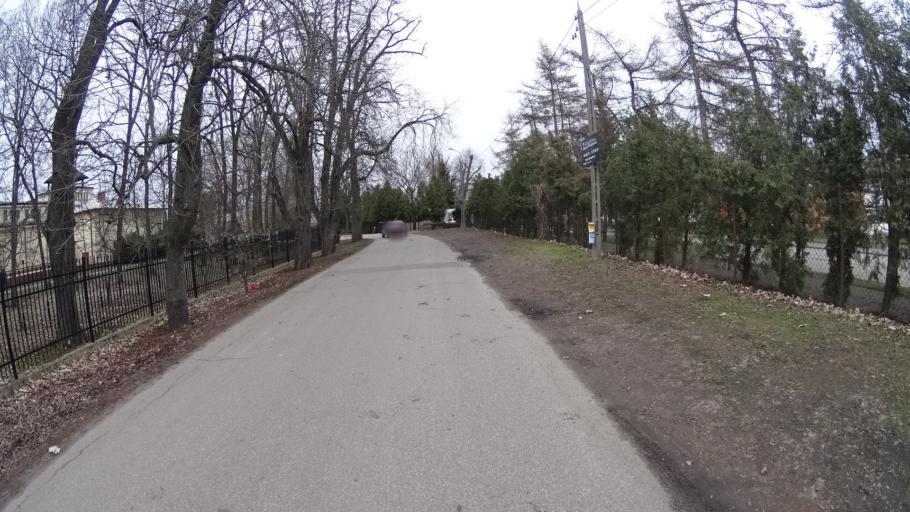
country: PL
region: Masovian Voivodeship
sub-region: Powiat warszawski zachodni
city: Jozefow
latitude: 52.2171
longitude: 20.6715
